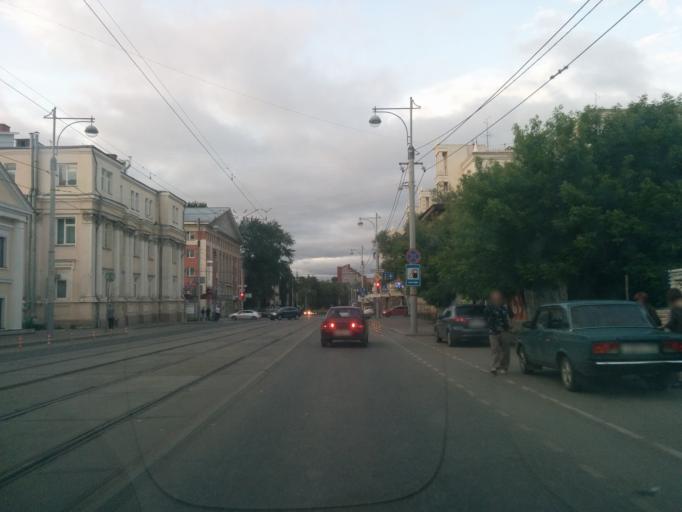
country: RU
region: Perm
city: Perm
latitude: 58.0158
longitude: 56.2546
